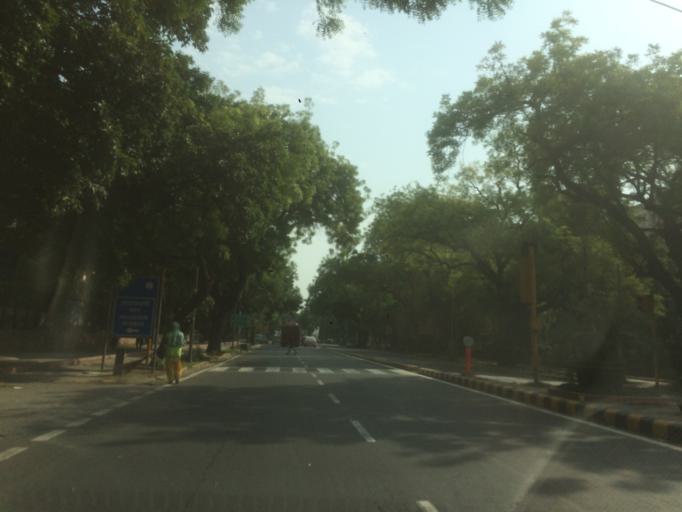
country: IN
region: NCT
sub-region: New Delhi
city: New Delhi
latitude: 28.6219
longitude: 77.2115
